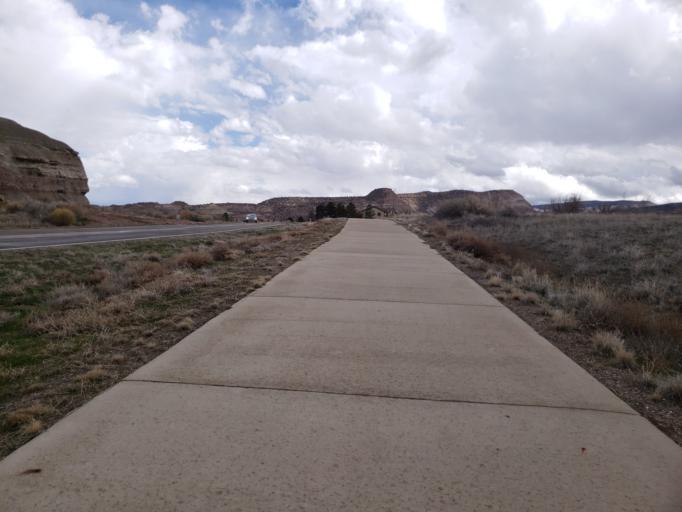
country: US
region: Colorado
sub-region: Mesa County
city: Redlands
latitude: 39.0455
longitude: -108.6338
